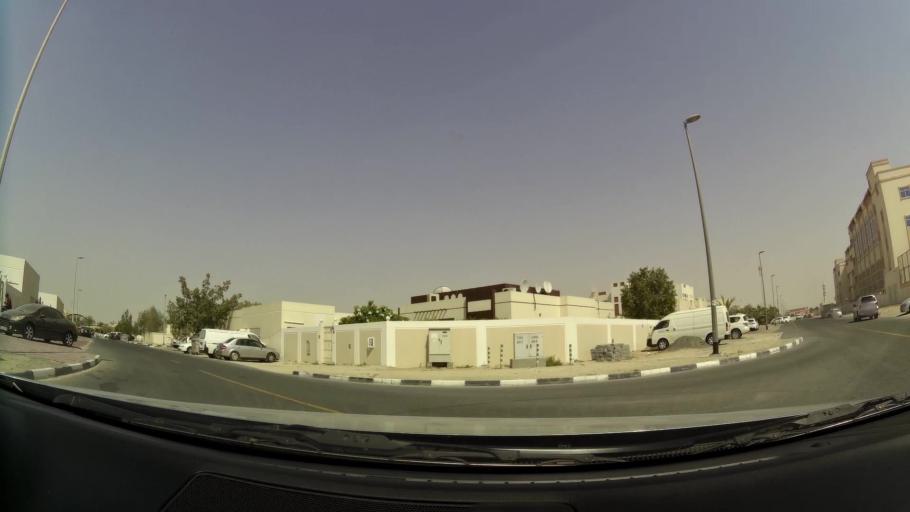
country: AE
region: Dubai
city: Dubai
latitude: 25.1513
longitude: 55.2536
